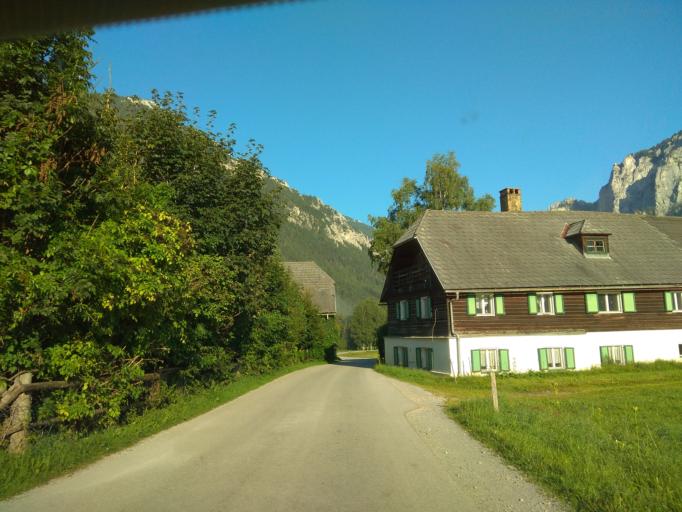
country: AT
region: Styria
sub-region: Politischer Bezirk Bruck-Muerzzuschlag
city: Sankt Ilgen
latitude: 47.5338
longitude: 15.0719
